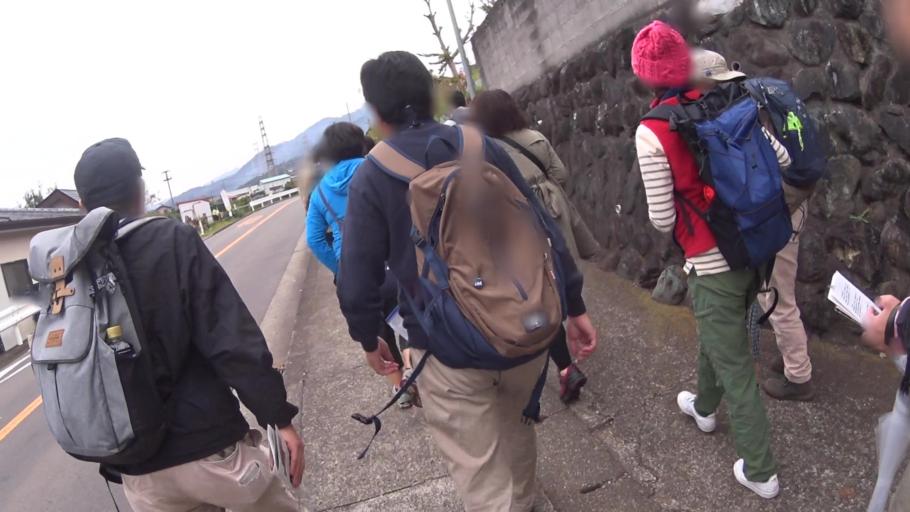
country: JP
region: Kanagawa
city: Hadano
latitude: 35.3938
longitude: 139.2344
